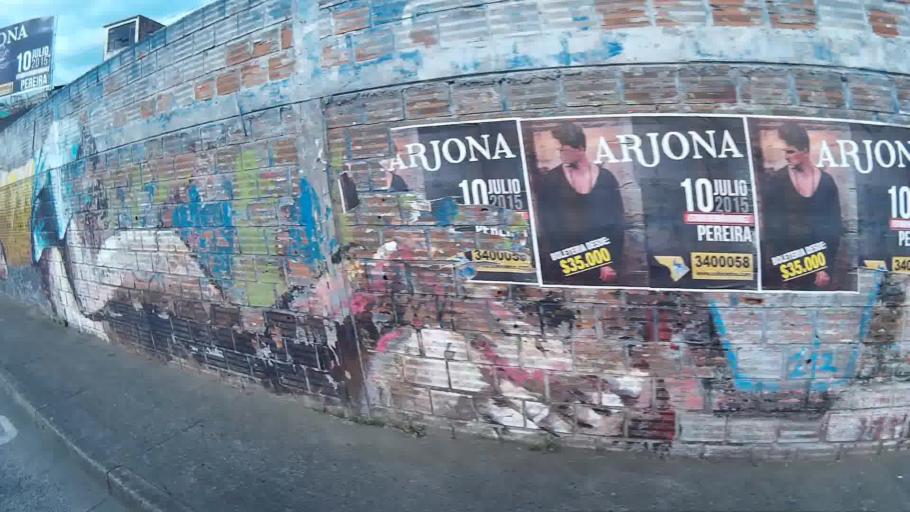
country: CO
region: Risaralda
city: Pereira
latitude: 4.8095
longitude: -75.6926
